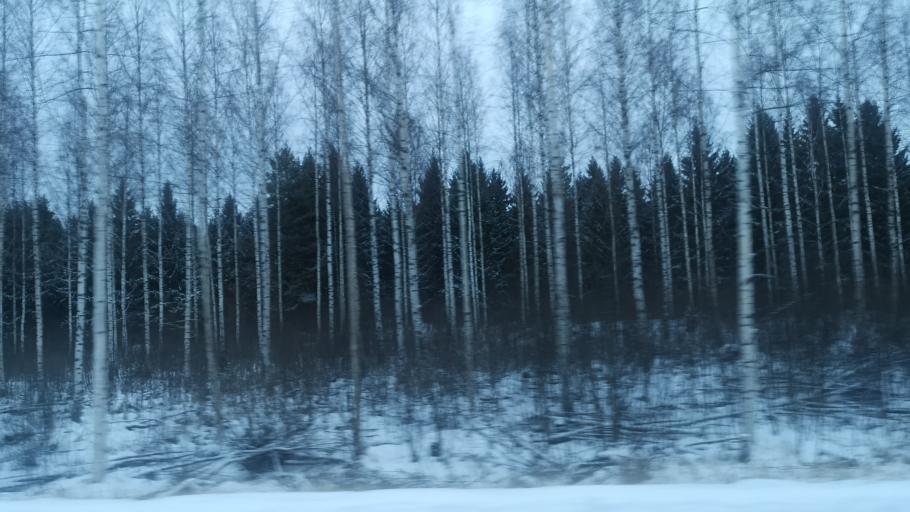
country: FI
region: Southern Savonia
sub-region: Savonlinna
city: Enonkoski
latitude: 62.1063
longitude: 28.6339
